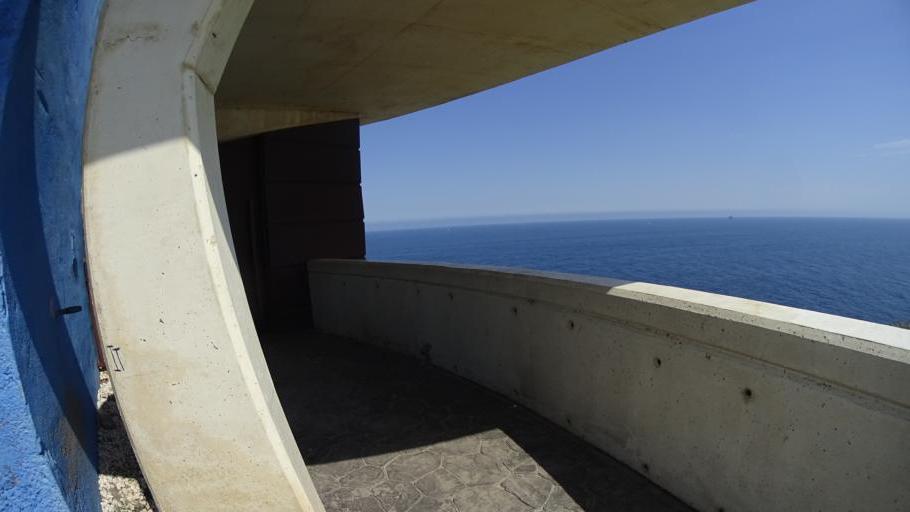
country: ES
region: Basque Country
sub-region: Bizkaia
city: Bermeo
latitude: 43.4553
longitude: -2.7527
